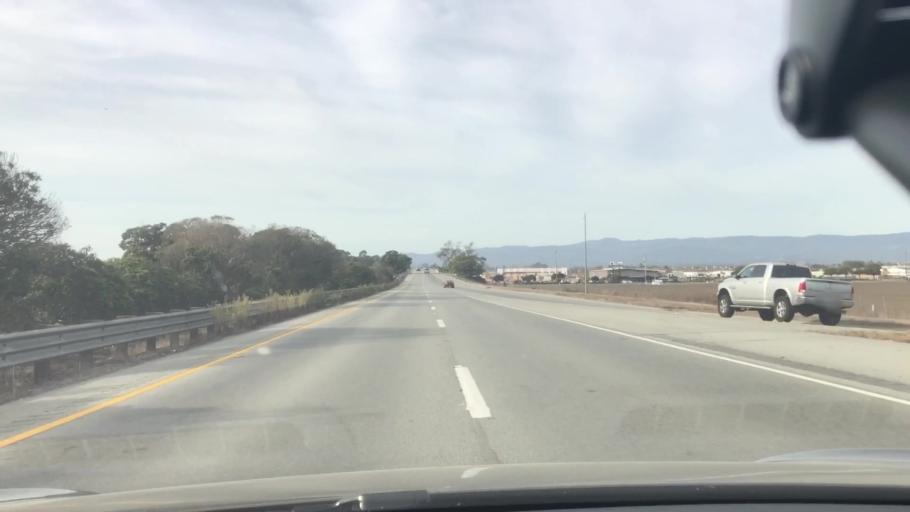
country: US
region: California
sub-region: Santa Cruz County
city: Watsonville
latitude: 36.8956
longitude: -121.7747
